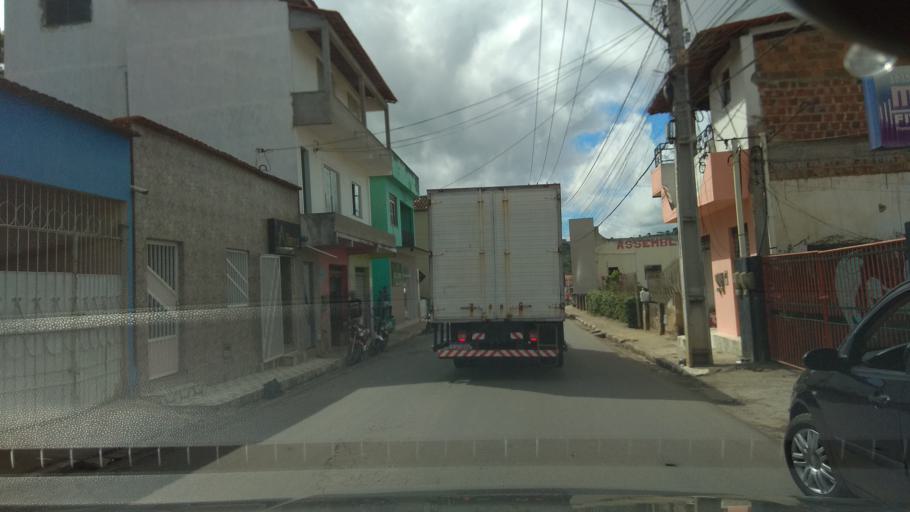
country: BR
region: Bahia
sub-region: Mutuipe
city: Mutuipe
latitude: -13.1810
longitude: -39.4201
